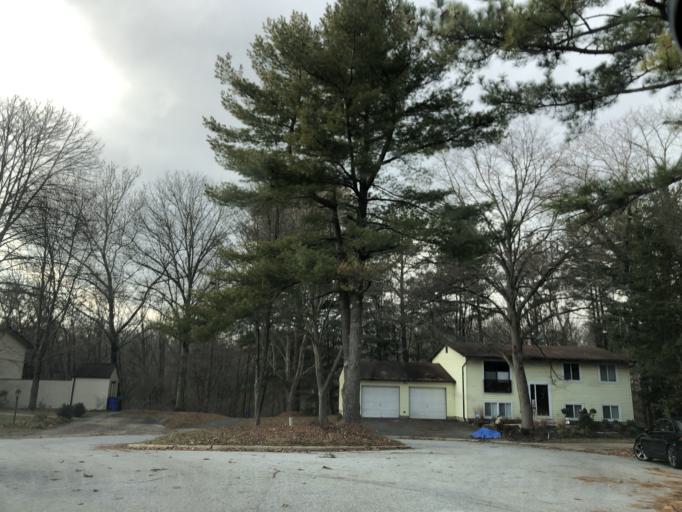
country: US
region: Maryland
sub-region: Howard County
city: Columbia
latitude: 39.2035
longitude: -76.8406
